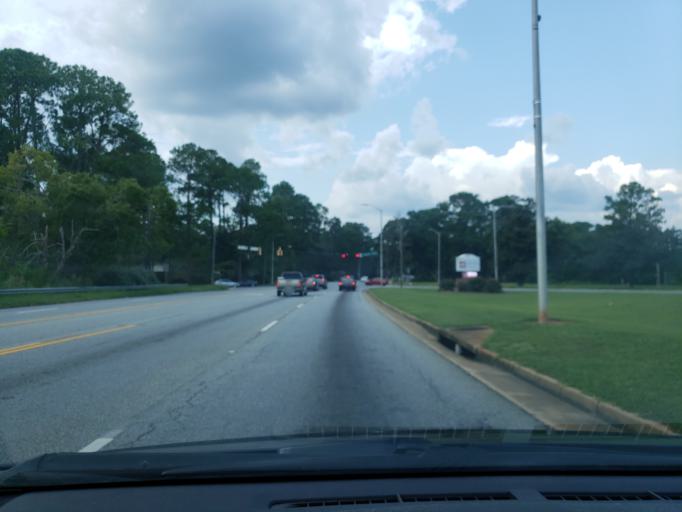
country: US
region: Georgia
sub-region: Dougherty County
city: Albany
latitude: 31.5908
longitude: -84.1907
